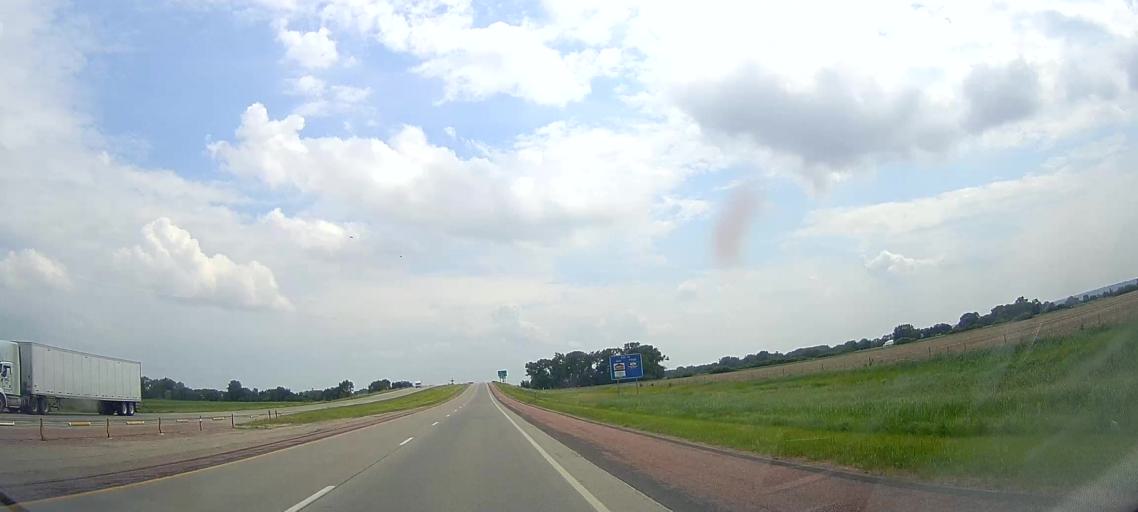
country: US
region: South Dakota
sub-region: Union County
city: Elk Point
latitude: 42.6987
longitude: -96.6974
